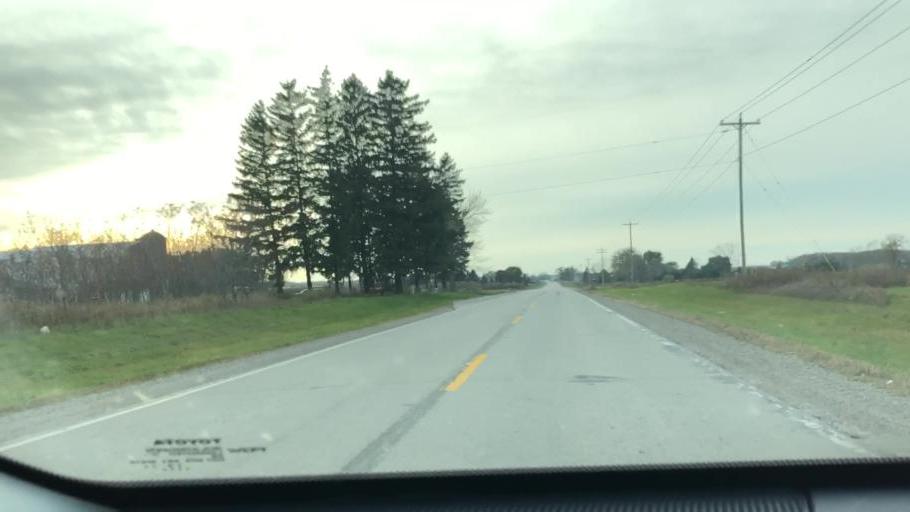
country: US
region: Wisconsin
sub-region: Outagamie County
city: Seymour
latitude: 44.4437
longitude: -88.3209
